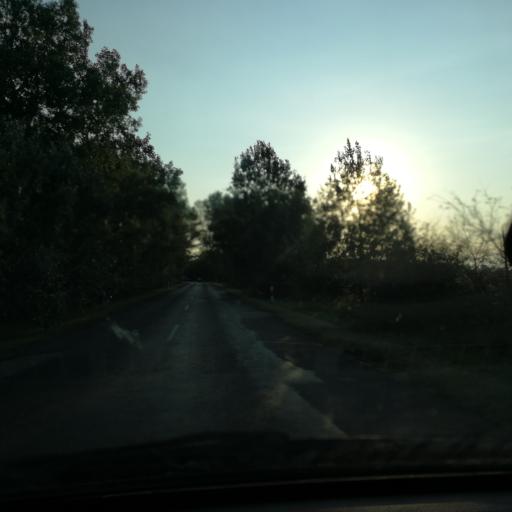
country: HU
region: Bacs-Kiskun
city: Szank
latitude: 46.4530
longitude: 19.6216
